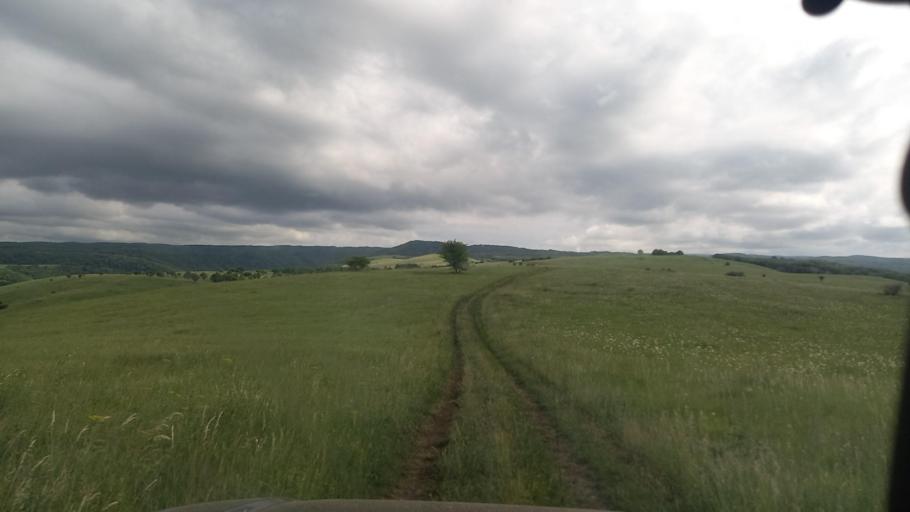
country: RU
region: Krasnodarskiy
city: Peredovaya
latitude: 44.0769
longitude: 41.3668
